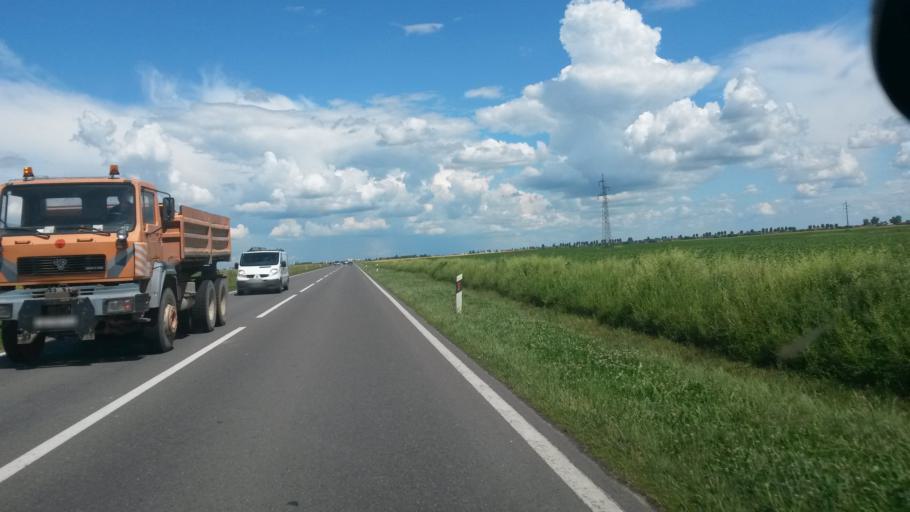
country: HR
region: Osjecko-Baranjska
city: Visnjevac
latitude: 45.5408
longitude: 18.5946
